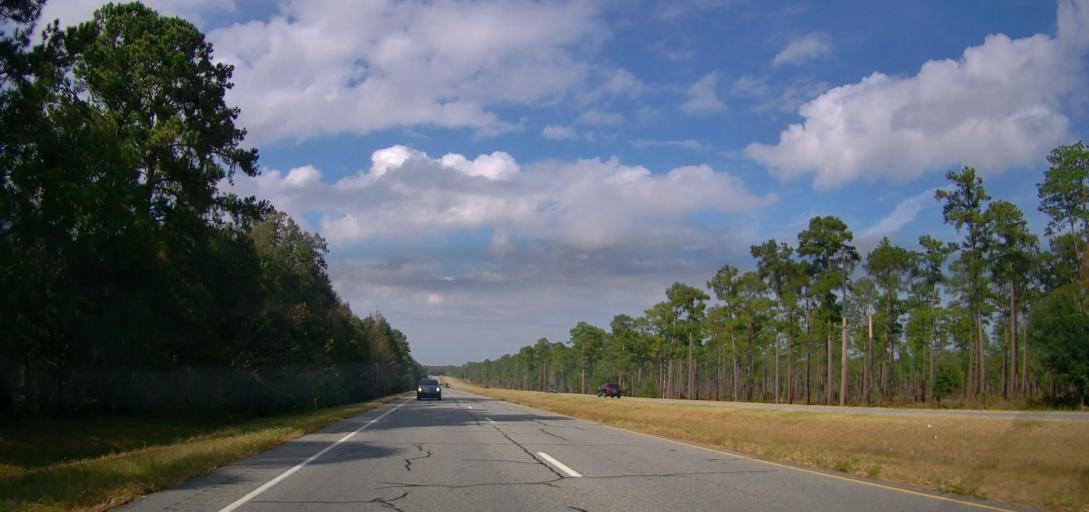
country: US
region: Georgia
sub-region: Mitchell County
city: Pelham
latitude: 31.1605
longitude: -84.1435
